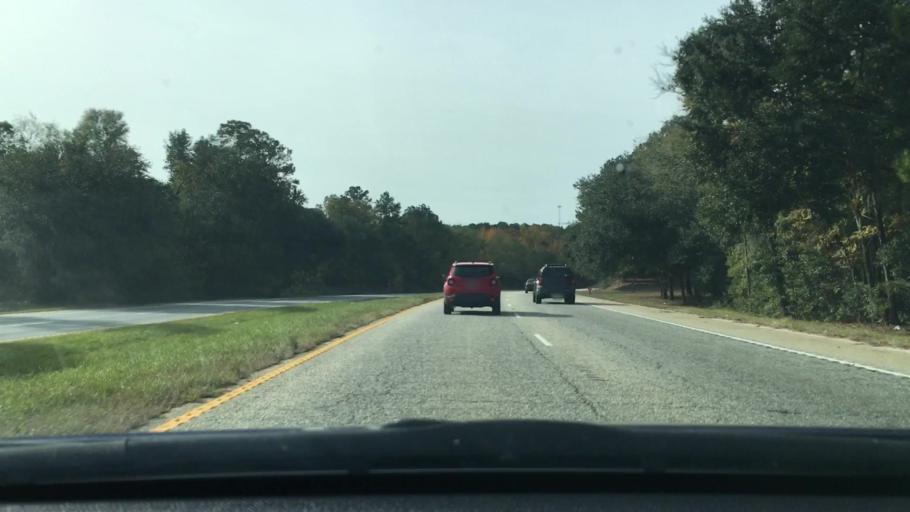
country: US
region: South Carolina
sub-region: Sumter County
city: Stateburg
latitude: 33.9453
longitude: -80.5150
